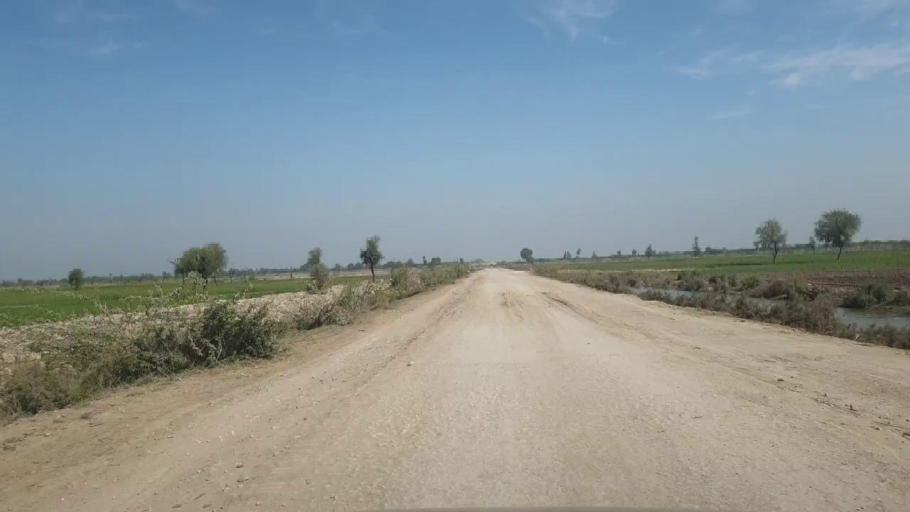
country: PK
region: Sindh
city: Samaro
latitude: 25.3144
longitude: 69.2303
